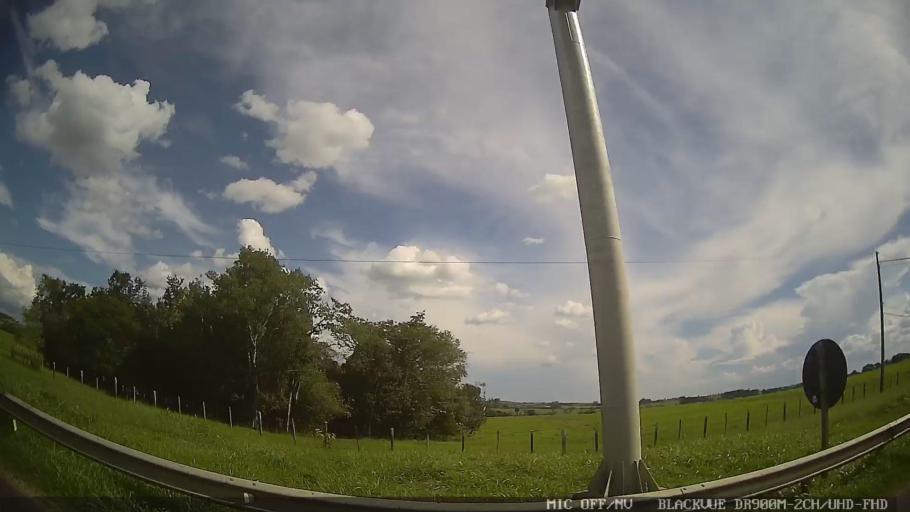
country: BR
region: Sao Paulo
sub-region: Conchas
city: Conchas
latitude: -23.0463
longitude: -47.9536
